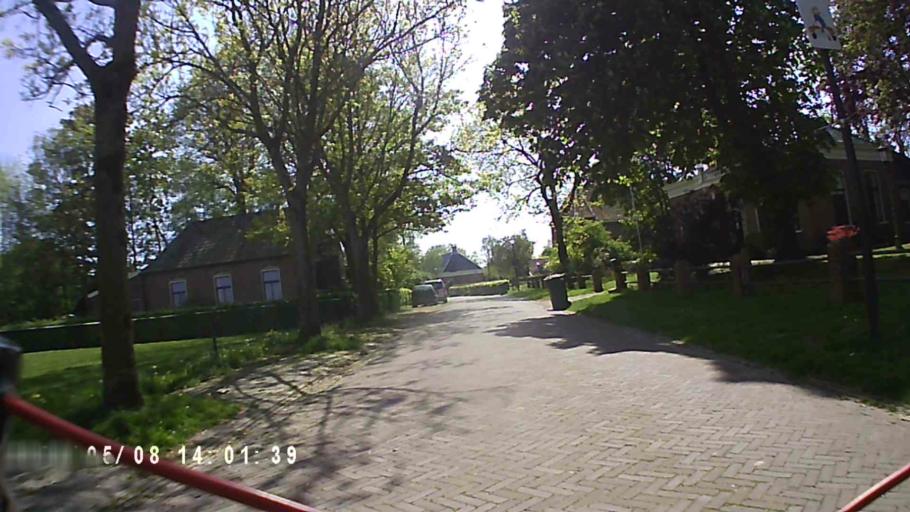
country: NL
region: Groningen
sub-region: Gemeente Appingedam
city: Appingedam
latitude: 53.3404
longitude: 6.8125
